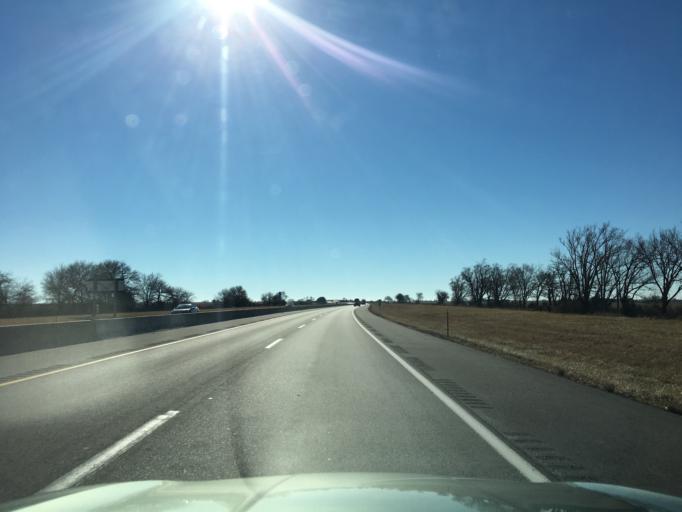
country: US
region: Kansas
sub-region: Sumner County
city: Wellington
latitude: 37.3179
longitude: -97.3397
